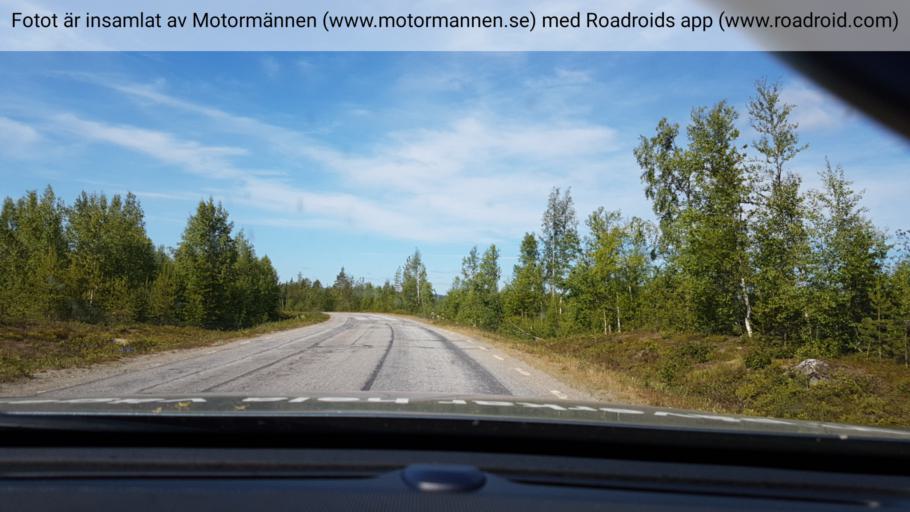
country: SE
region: Vaesterbotten
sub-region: Dorotea Kommun
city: Dorotea
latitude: 64.3692
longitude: 16.1731
